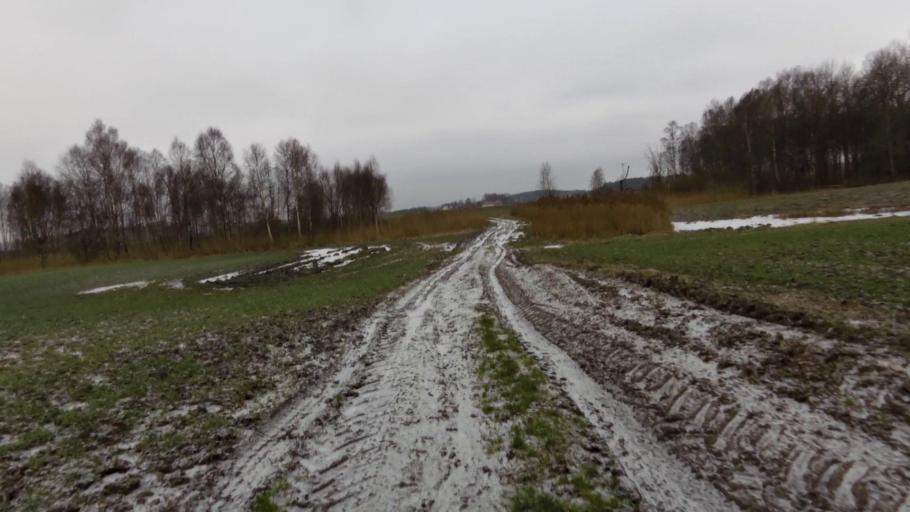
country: PL
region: West Pomeranian Voivodeship
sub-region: Powiat szczecinecki
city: Szczecinek
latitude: 53.6463
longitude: 16.6194
